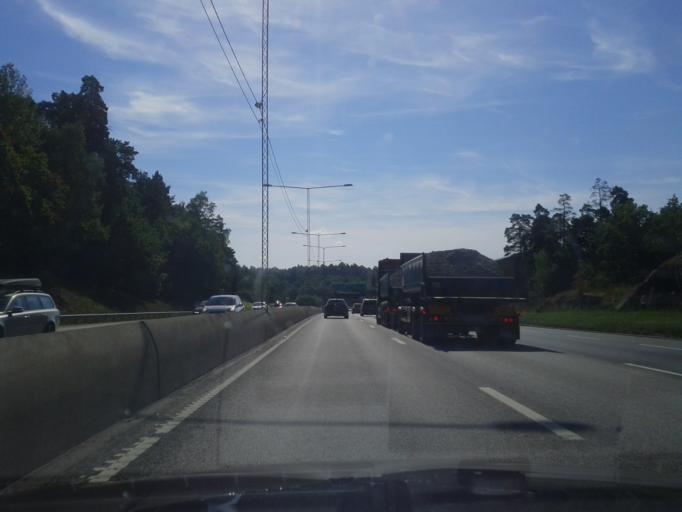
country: SE
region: Stockholm
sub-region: Norrtalje Kommun
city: Bergshamra
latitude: 59.3957
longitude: 18.0393
